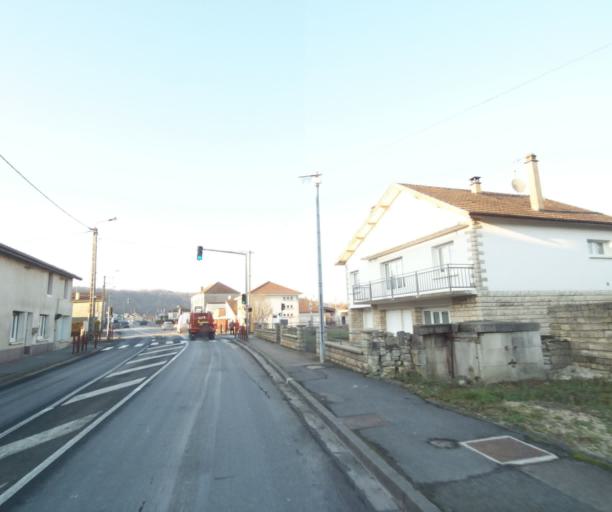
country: FR
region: Champagne-Ardenne
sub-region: Departement de la Haute-Marne
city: Chevillon
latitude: 48.5253
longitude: 5.1025
